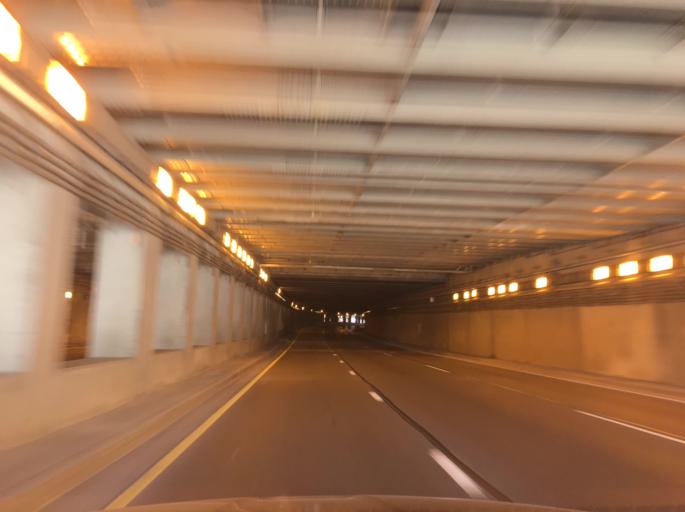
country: US
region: Michigan
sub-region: Wayne County
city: Detroit
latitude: 42.3273
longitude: -83.0479
